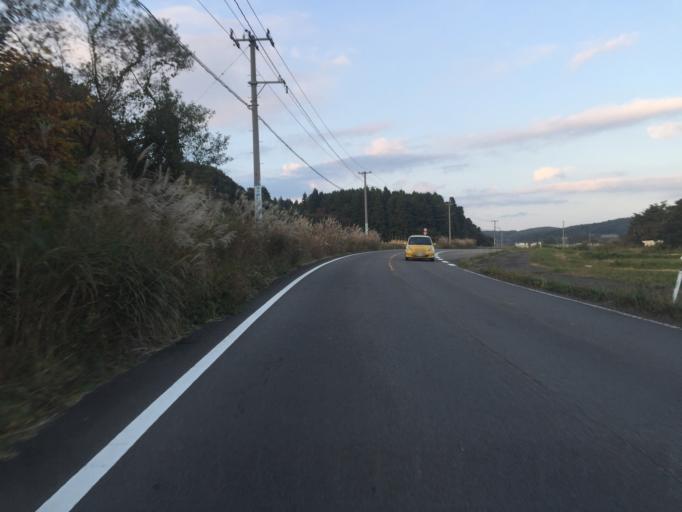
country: JP
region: Fukushima
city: Nihommatsu
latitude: 37.5862
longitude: 140.3527
